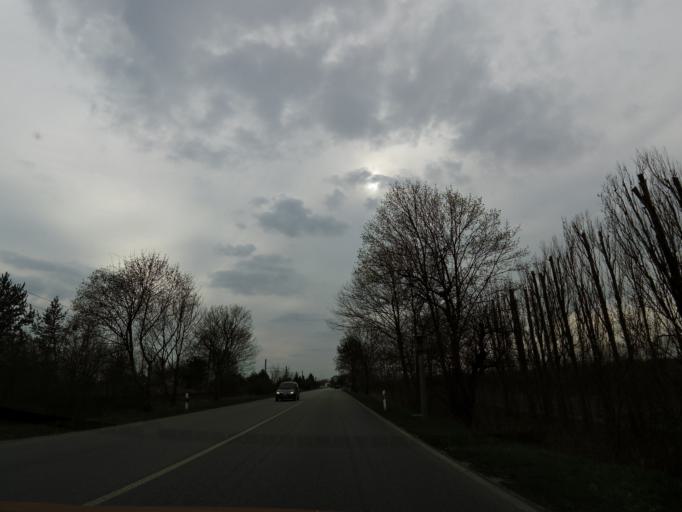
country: DE
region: Brandenburg
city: Mullrose
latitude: 52.3009
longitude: 14.4780
